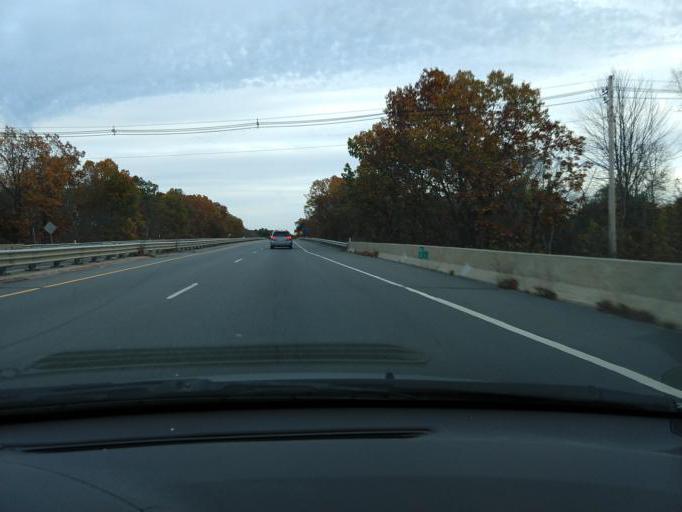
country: US
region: Massachusetts
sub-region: Middlesex County
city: Littleton Common
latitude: 42.5187
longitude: -71.5038
